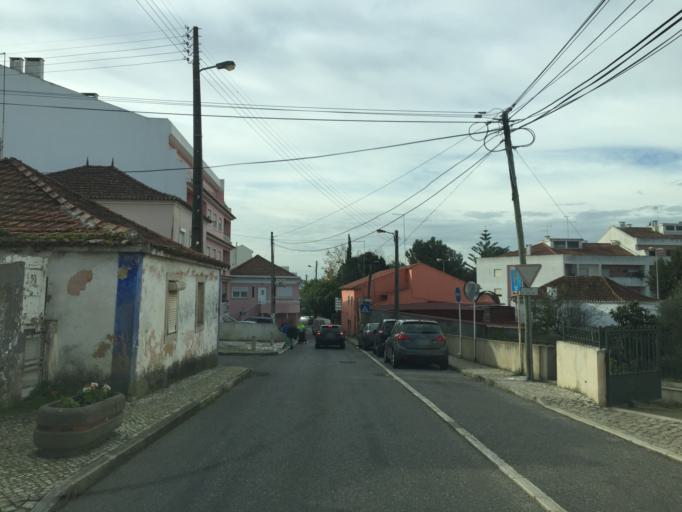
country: PT
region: Lisbon
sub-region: Sintra
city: Pero Pinheiro
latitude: 38.8579
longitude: -9.3254
